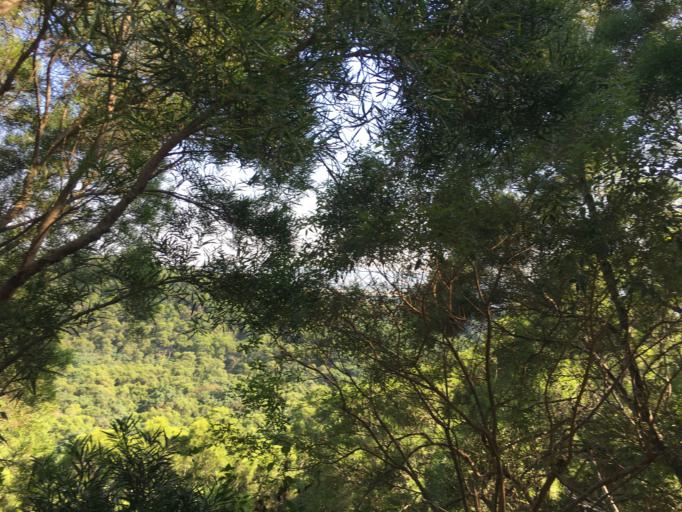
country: TW
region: Taiwan
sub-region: Changhua
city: Chang-hua
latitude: 24.1469
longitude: 120.5583
